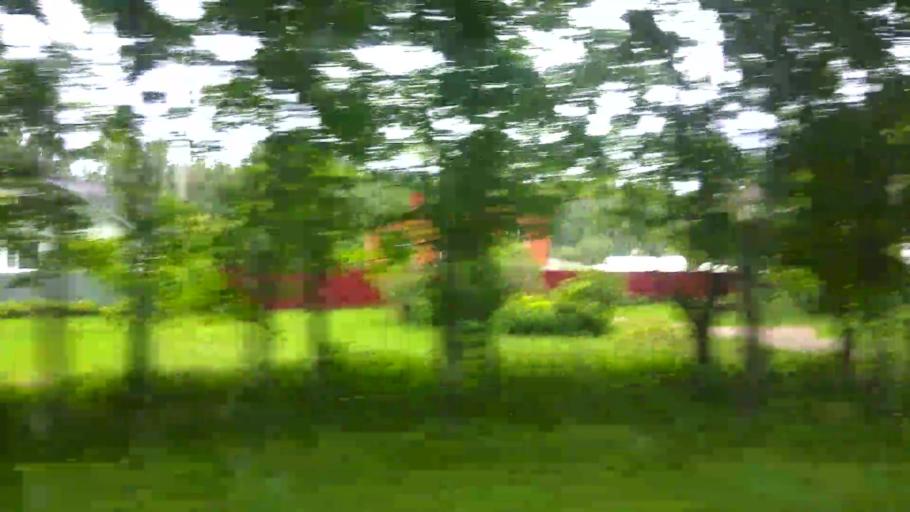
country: RU
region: Moskovskaya
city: Ozherel'ye
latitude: 54.8352
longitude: 38.2780
